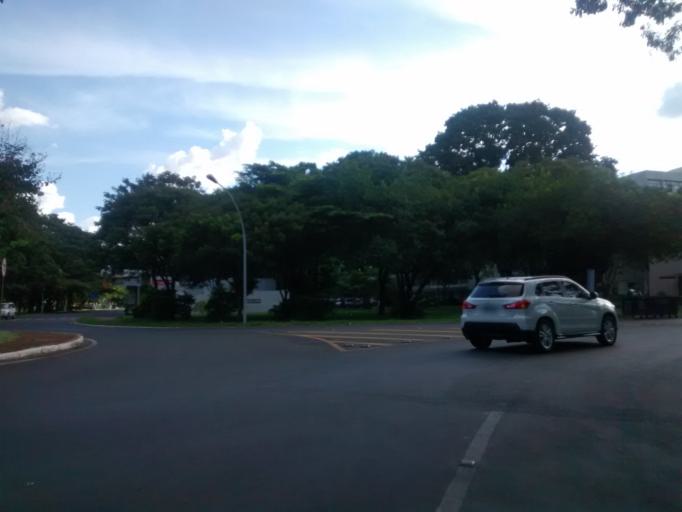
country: BR
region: Federal District
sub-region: Brasilia
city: Brasilia
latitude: -15.8083
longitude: -47.8961
